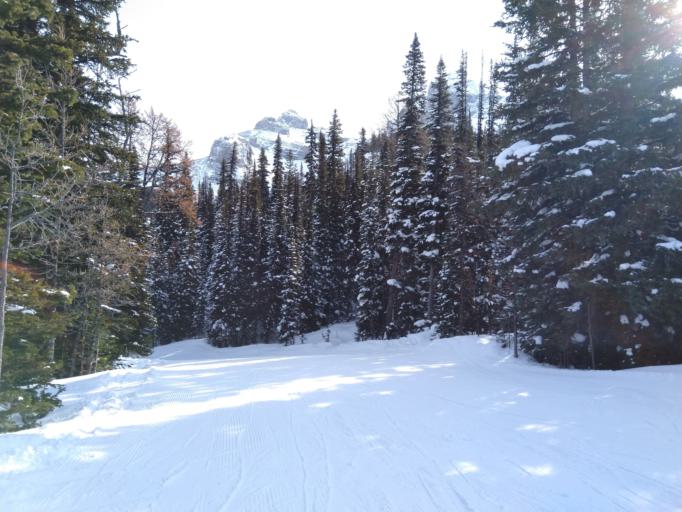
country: CA
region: Alberta
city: Banff
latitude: 51.0855
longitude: -115.7688
